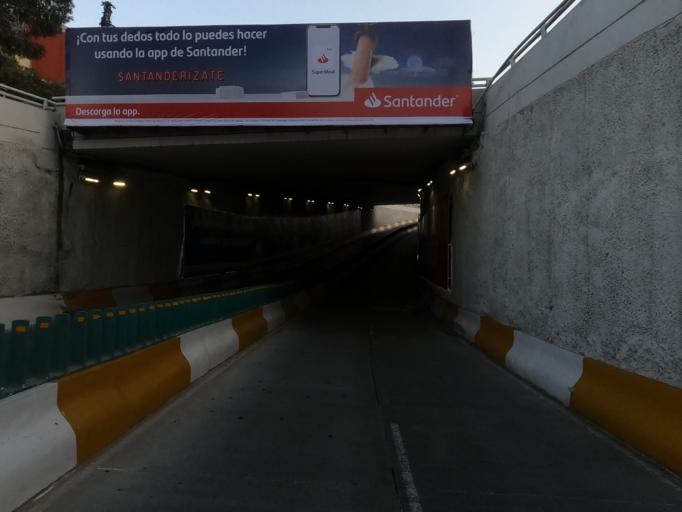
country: MX
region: Mexico
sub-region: Huixquilucan
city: Naucalpan de Juarez
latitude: 19.4059
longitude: -99.2719
